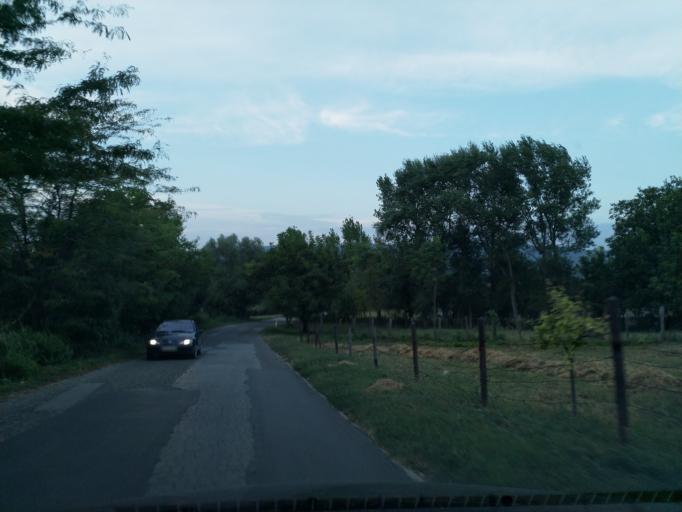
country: RS
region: Central Serbia
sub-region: Pomoravski Okrug
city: Paracin
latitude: 43.8539
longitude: 21.5287
